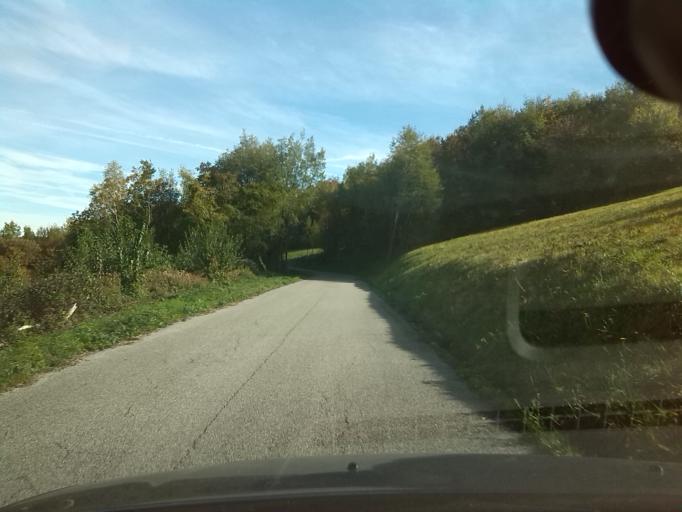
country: IT
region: Friuli Venezia Giulia
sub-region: Provincia di Udine
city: San Leonardo
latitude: 46.1003
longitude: 13.5360
